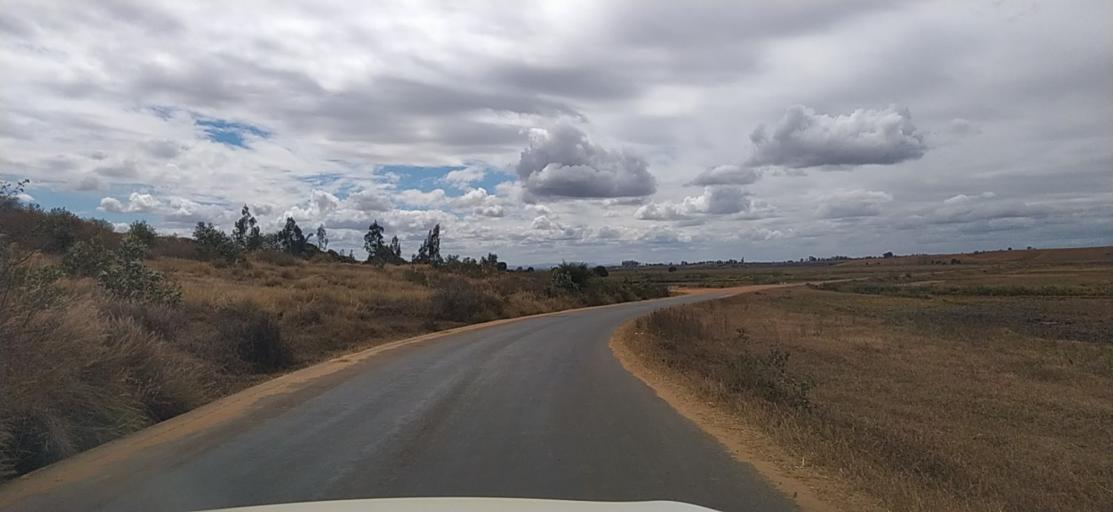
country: MG
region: Alaotra Mangoro
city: Ambatondrazaka
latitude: -17.9227
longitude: 48.2578
